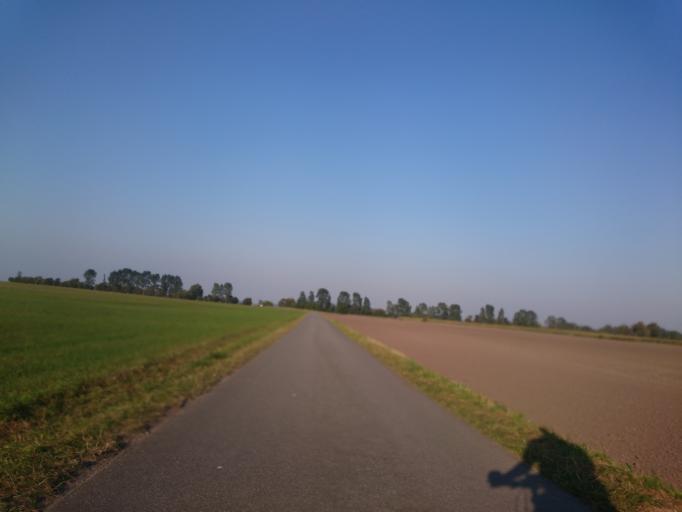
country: DE
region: Mecklenburg-Vorpommern
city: Velgast
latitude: 54.3393
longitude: 12.8180
